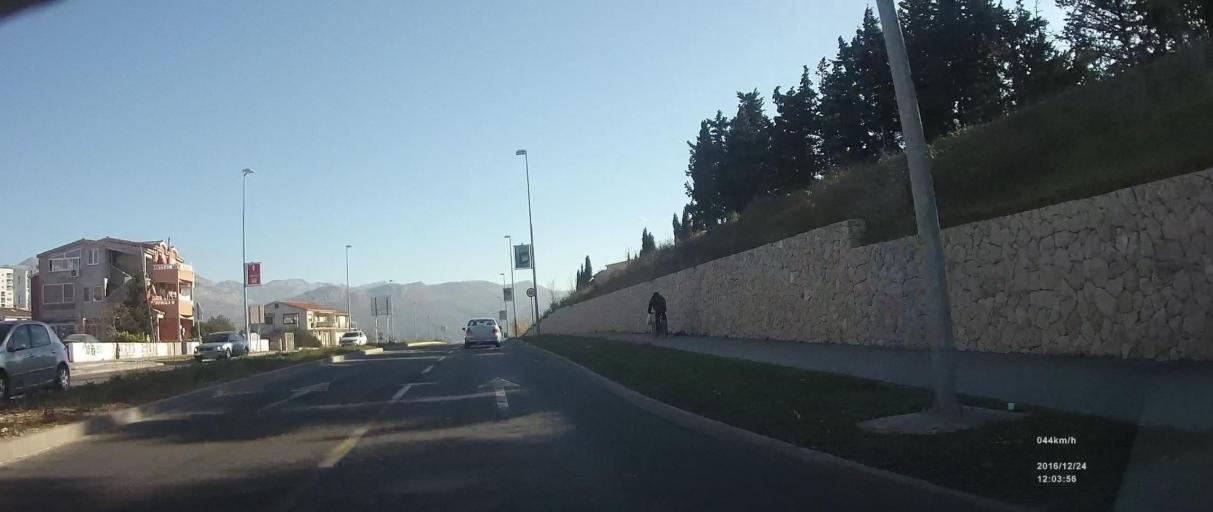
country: HR
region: Splitsko-Dalmatinska
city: Kamen
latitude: 43.5149
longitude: 16.4938
